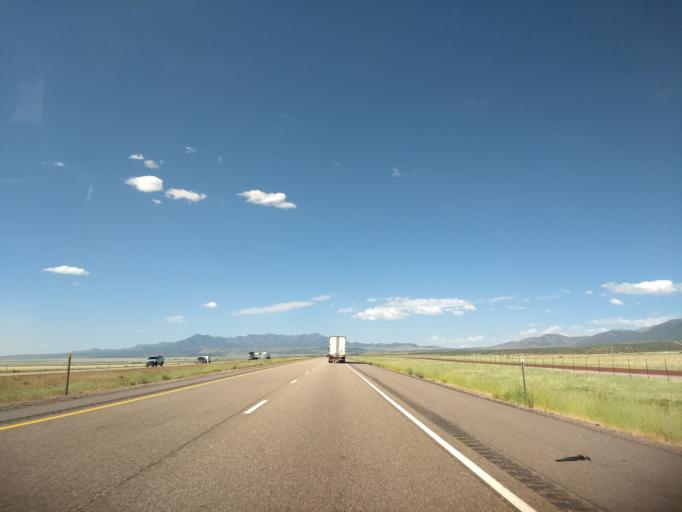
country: US
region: Utah
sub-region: Millard County
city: Fillmore
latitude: 39.0448
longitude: -112.2930
